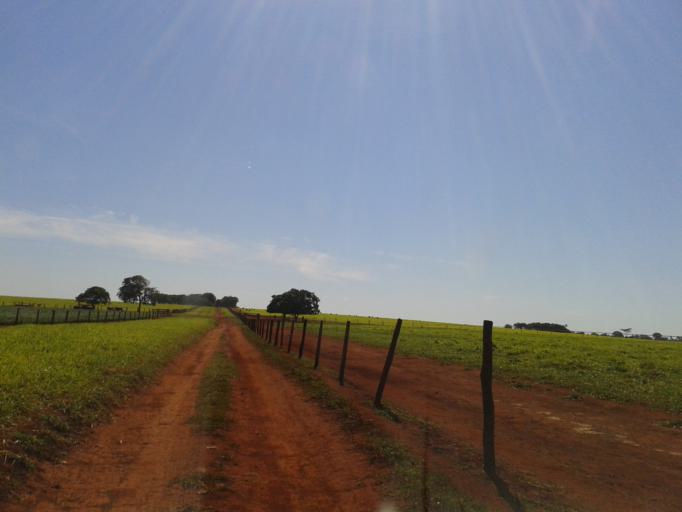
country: BR
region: Minas Gerais
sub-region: Centralina
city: Centralina
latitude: -18.6525
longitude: -49.2771
